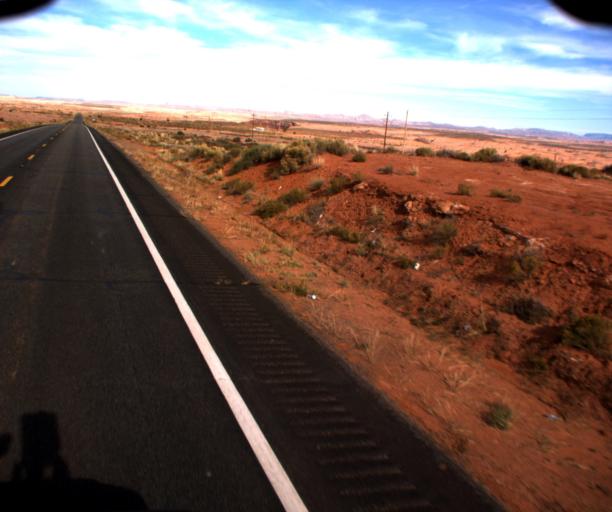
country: US
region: Arizona
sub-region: Navajo County
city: Kayenta
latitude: 36.9266
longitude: -109.7549
